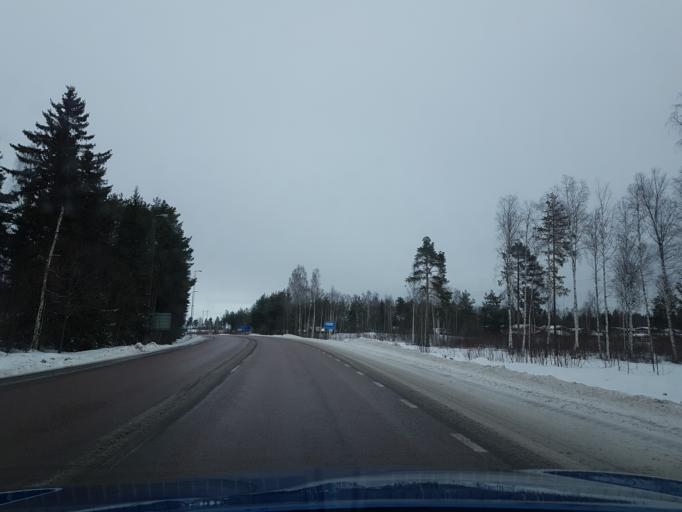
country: SE
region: Dalarna
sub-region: Mora Kommun
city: Mora
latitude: 61.0119
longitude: 14.5906
